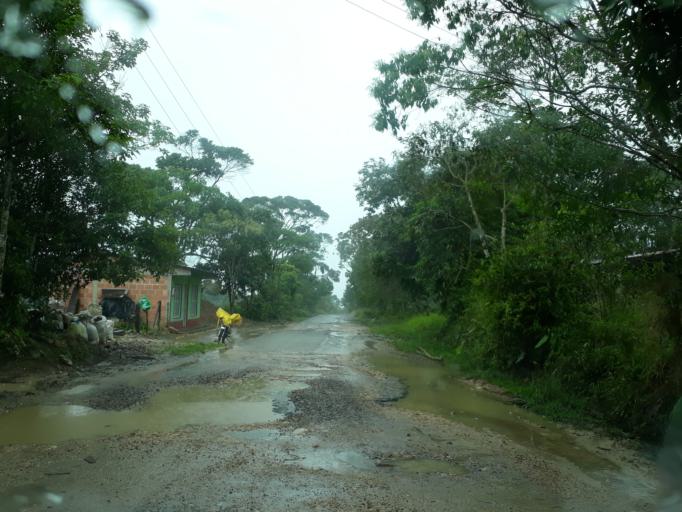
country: CO
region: Cundinamarca
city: Medina
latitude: 4.6515
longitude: -73.3299
